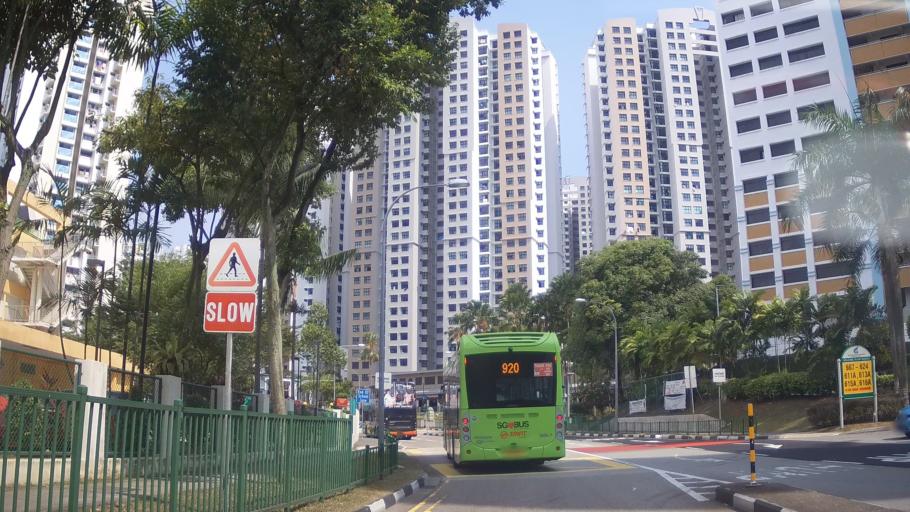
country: MY
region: Johor
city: Johor Bahru
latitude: 1.3840
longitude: 103.7605
